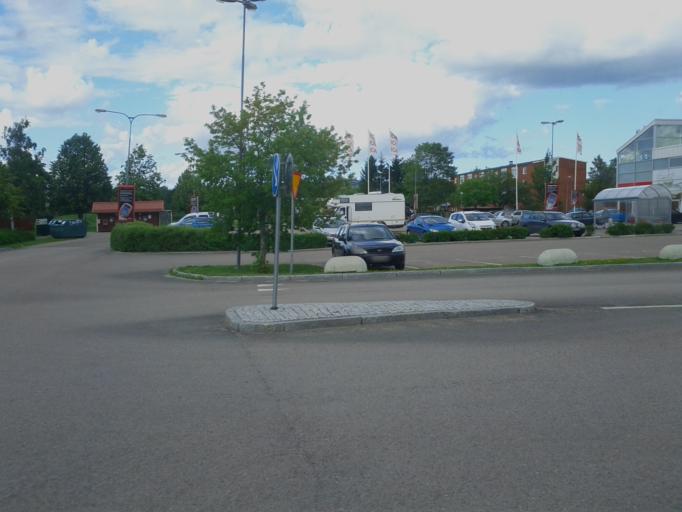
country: SE
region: Vaestmanland
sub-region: Sala Kommun
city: Sala
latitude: 59.9226
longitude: 16.5856
